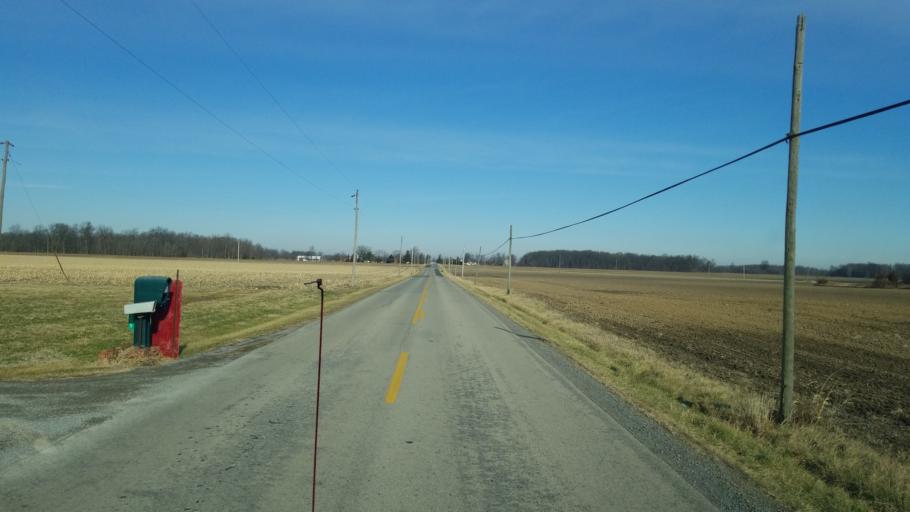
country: US
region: Ohio
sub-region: Allen County
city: Bluffton
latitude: 40.8597
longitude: -83.8991
